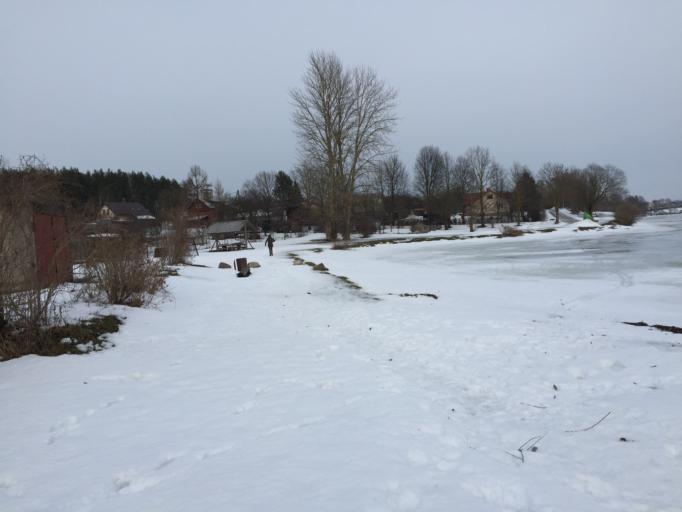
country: LV
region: Salaspils
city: Salaspils
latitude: 56.8414
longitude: 24.4310
